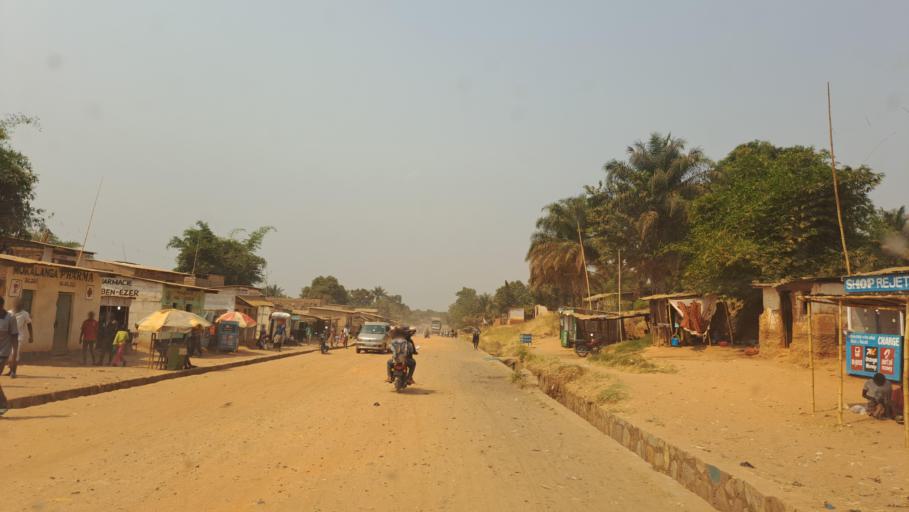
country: CD
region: Kasai-Oriental
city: Mbuji-Mayi
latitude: -6.1070
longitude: 23.5605
